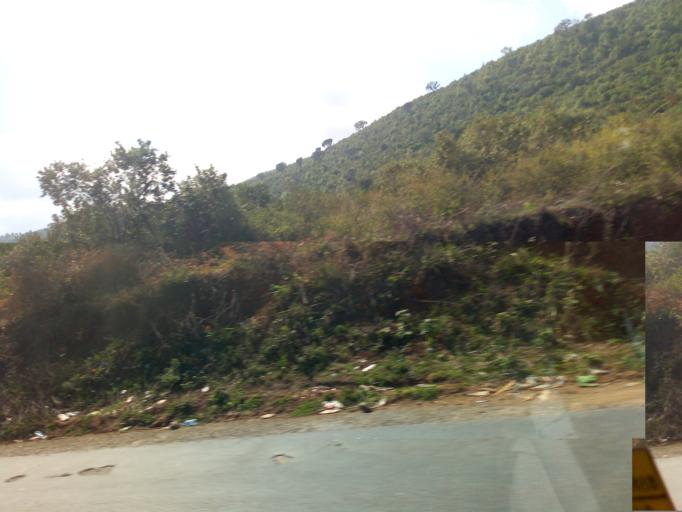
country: KE
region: Nakuru
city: Kijabe
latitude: -1.0082
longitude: 36.6020
